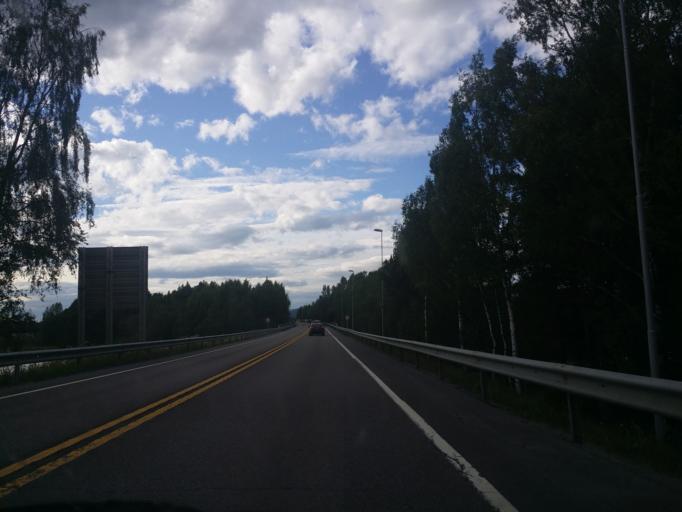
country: NO
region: Hedmark
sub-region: Hamar
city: Hamar
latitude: 60.7932
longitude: 11.1231
